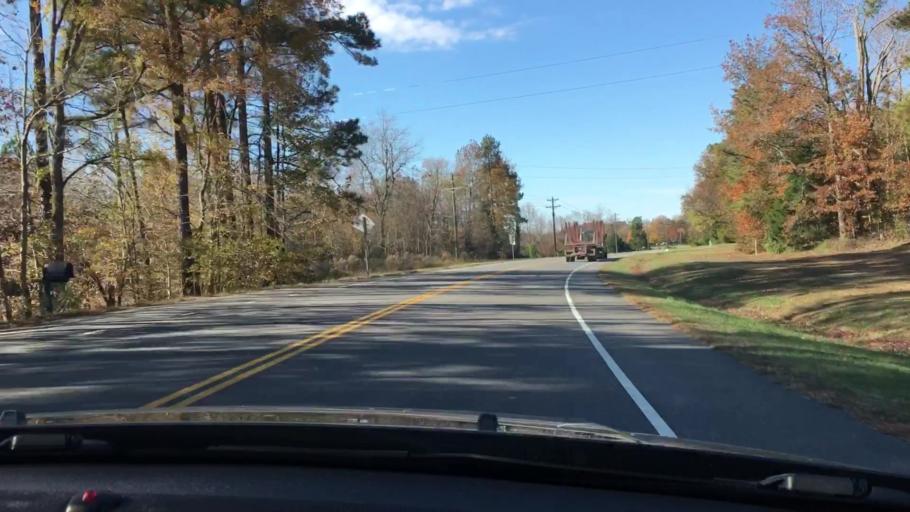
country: US
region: Virginia
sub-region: Hanover County
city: Hanover
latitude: 37.8004
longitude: -77.2606
